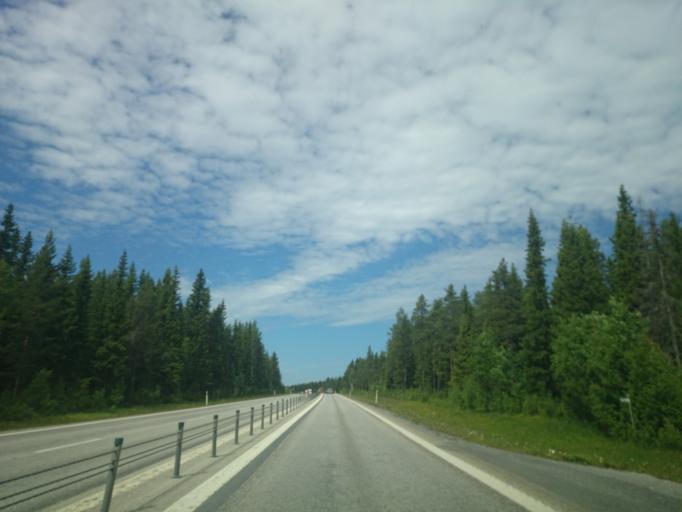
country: SE
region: Jaemtland
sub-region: OEstersunds Kommun
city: Brunflo
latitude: 63.1472
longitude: 14.7783
